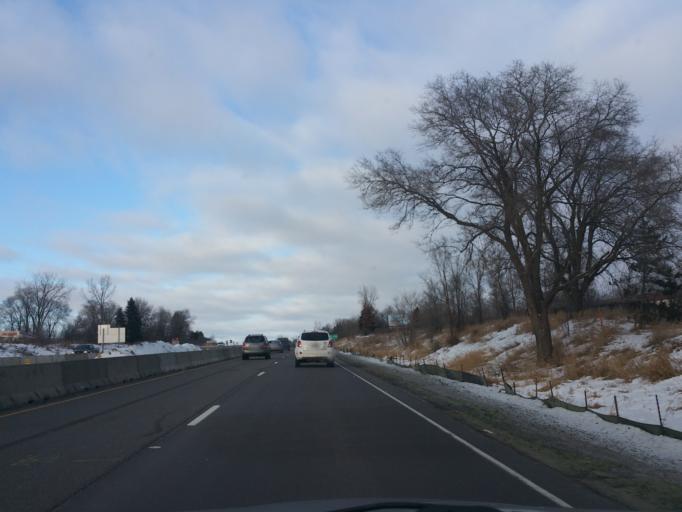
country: US
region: Minnesota
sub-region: Ramsey County
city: Vadnais Heights
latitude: 45.0698
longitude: -93.0538
